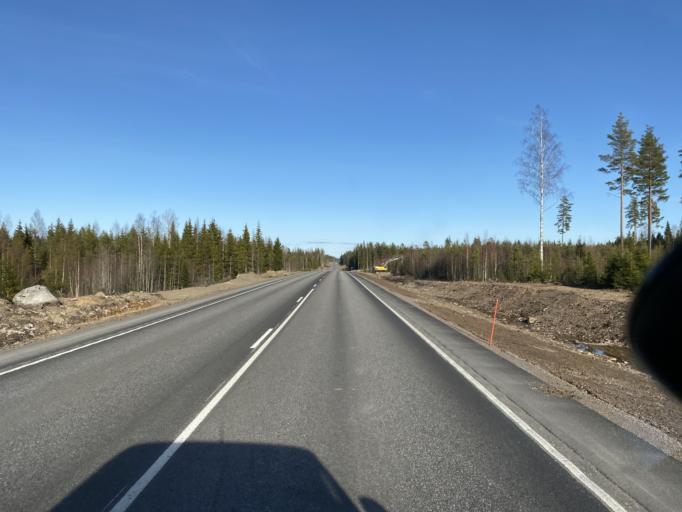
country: FI
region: Satakunta
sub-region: Pori
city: Kokemaeki
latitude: 61.1712
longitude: 22.4860
